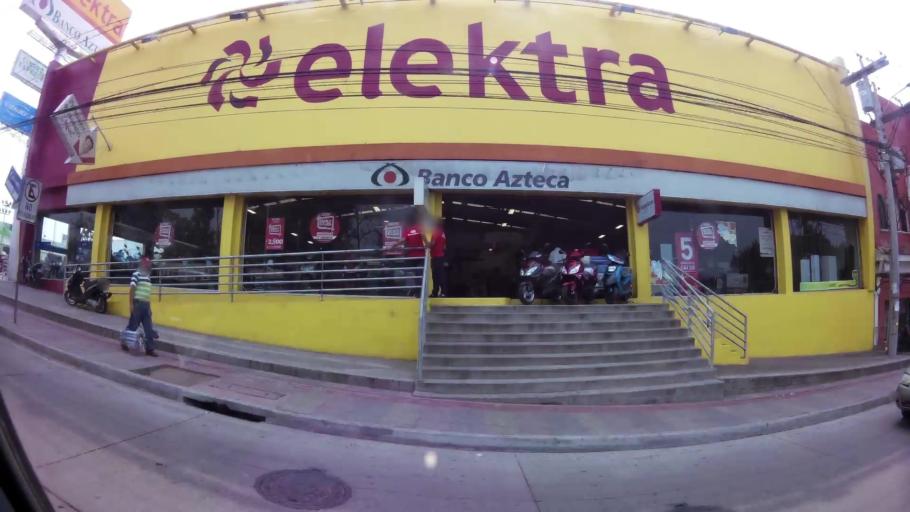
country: HN
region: Francisco Morazan
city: Tegucigalpa
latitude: 14.0689
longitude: -87.1843
